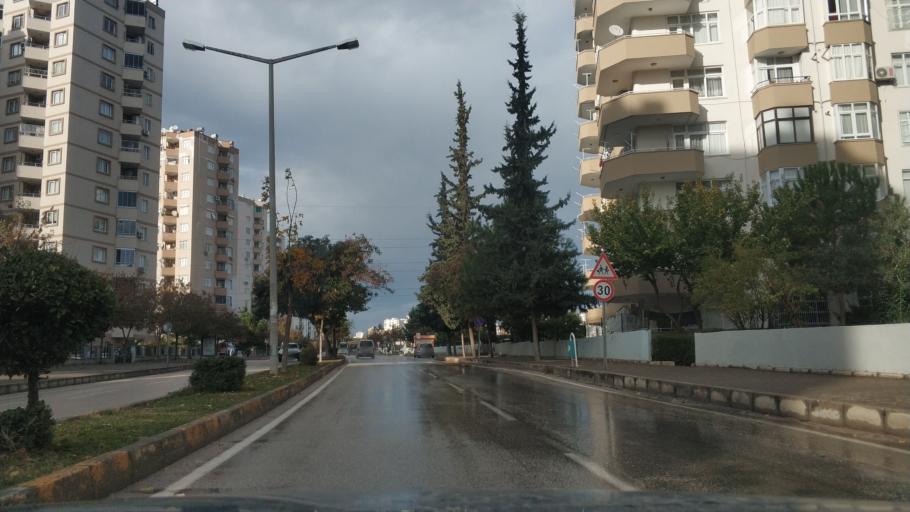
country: TR
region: Adana
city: Seyhan
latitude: 37.0376
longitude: 35.2615
